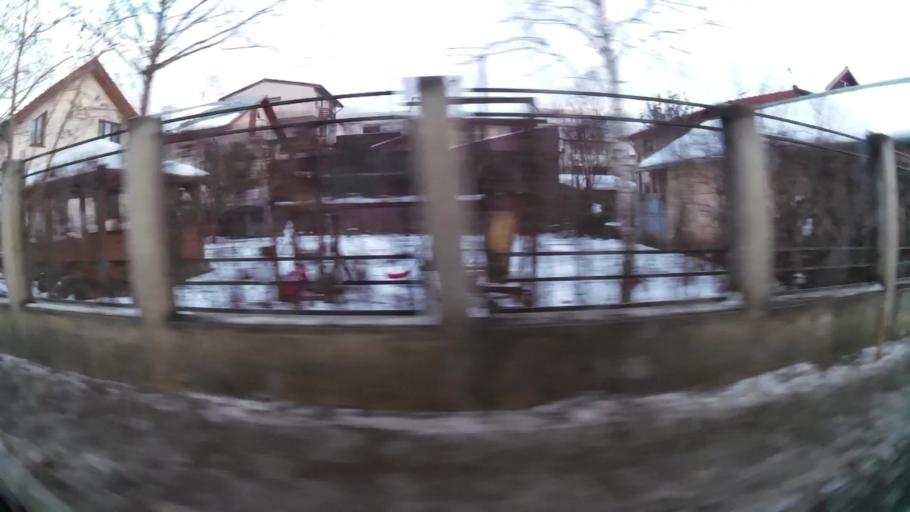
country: RO
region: Ilfov
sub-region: Comuna Popesti-Leordeni
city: Popesti-Leordeni
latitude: 44.3758
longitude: 26.1567
